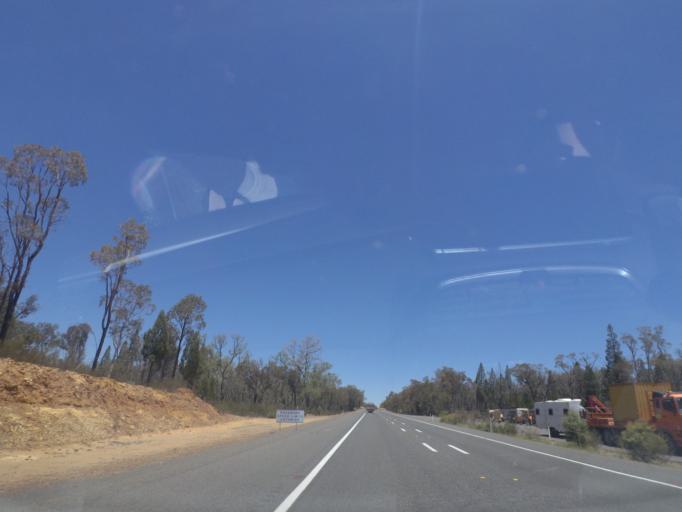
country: AU
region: New South Wales
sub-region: Warrumbungle Shire
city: Coonabarabran
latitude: -30.9189
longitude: 149.4333
